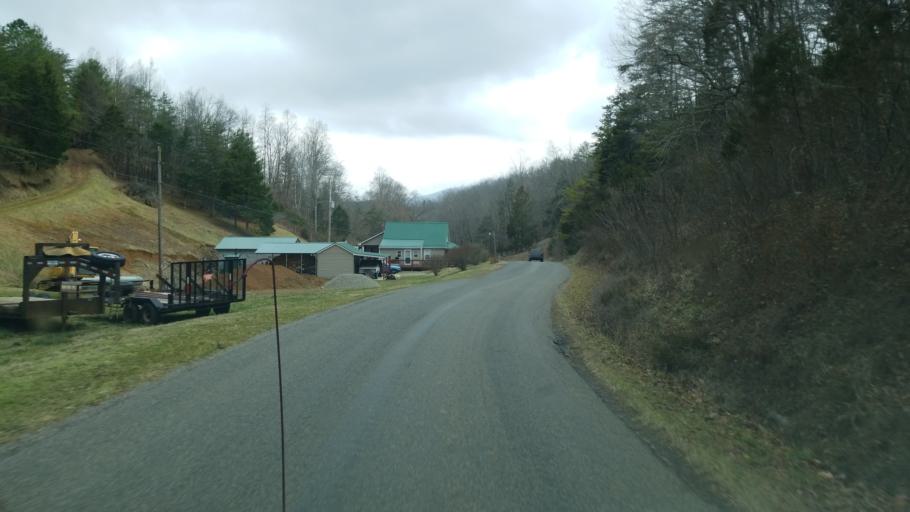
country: US
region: Virginia
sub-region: Giles County
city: Pearisburg
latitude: 37.2323
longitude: -80.6981
